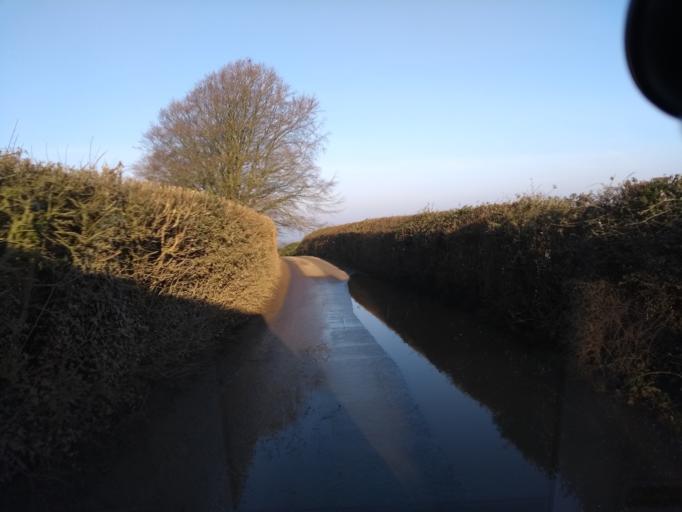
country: GB
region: England
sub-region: Somerset
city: Crewkerne
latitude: 50.8371
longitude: -2.8060
